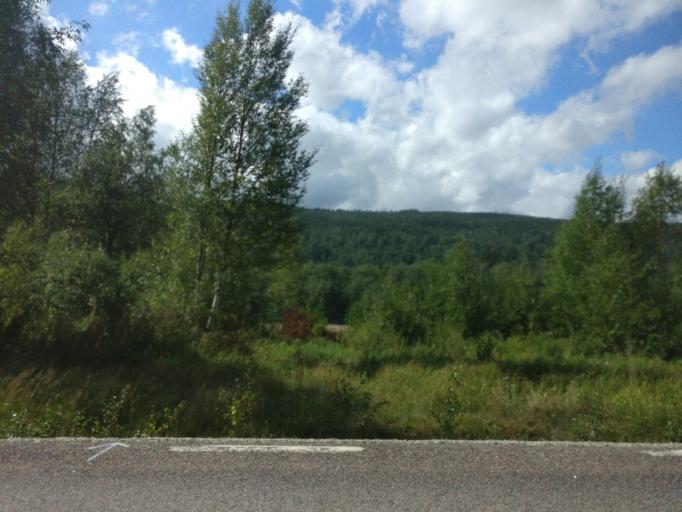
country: SE
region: Vaermland
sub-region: Hagfors Kommun
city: Ekshaerad
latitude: 60.3659
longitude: 13.3085
